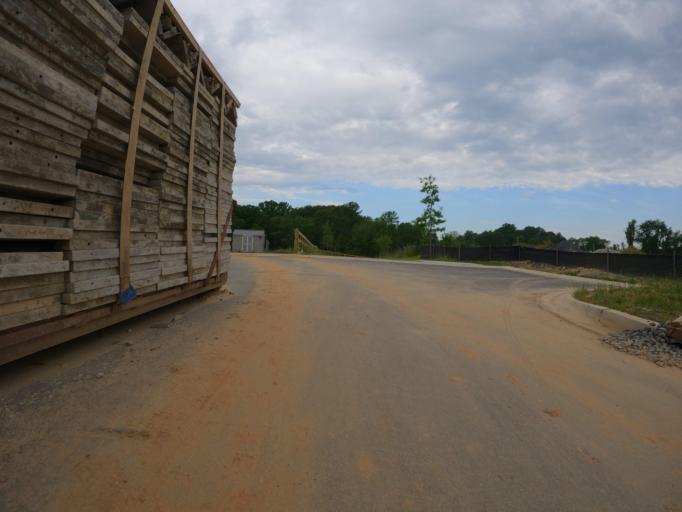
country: US
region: Maryland
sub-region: Howard County
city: Highland
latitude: 39.2333
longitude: -77.0028
